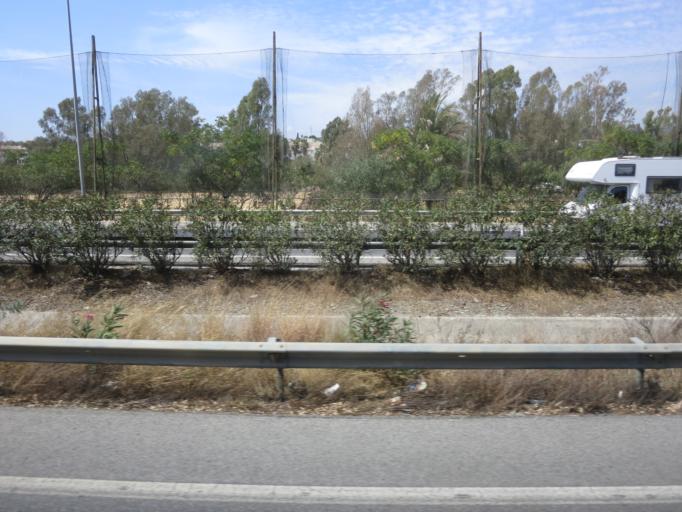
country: ES
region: Andalusia
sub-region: Provincia de Malaga
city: Marbella
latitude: 36.5016
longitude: -4.9471
